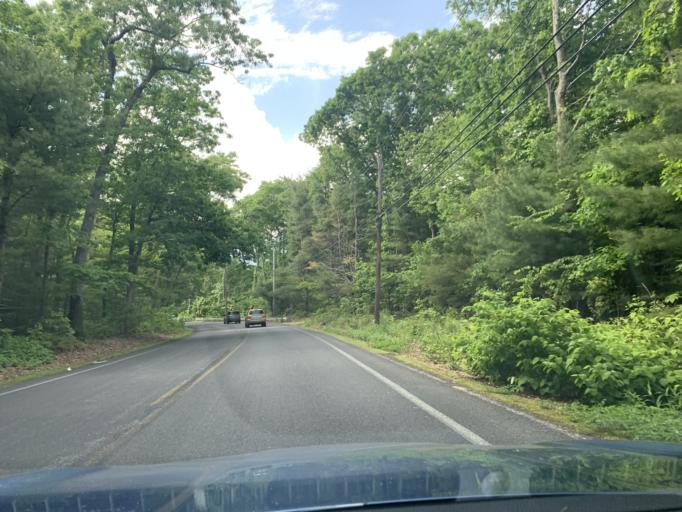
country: US
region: Rhode Island
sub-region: Kent County
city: Coventry
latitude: 41.6845
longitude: -71.6709
